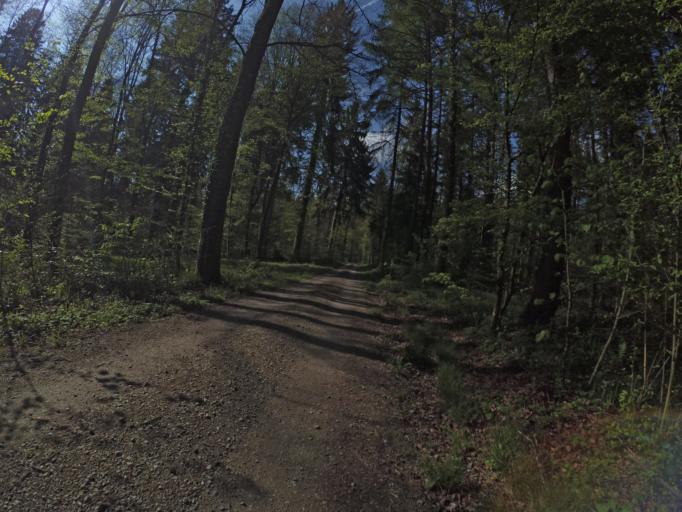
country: CH
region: Thurgau
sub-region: Frauenfeld District
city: Diessenhofen
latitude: 47.6555
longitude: 8.7557
